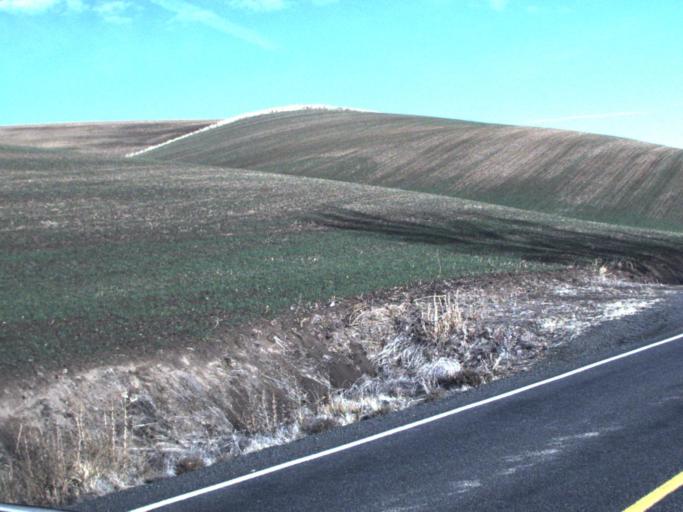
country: US
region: Washington
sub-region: Whitman County
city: Colfax
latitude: 46.7642
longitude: -117.4143
